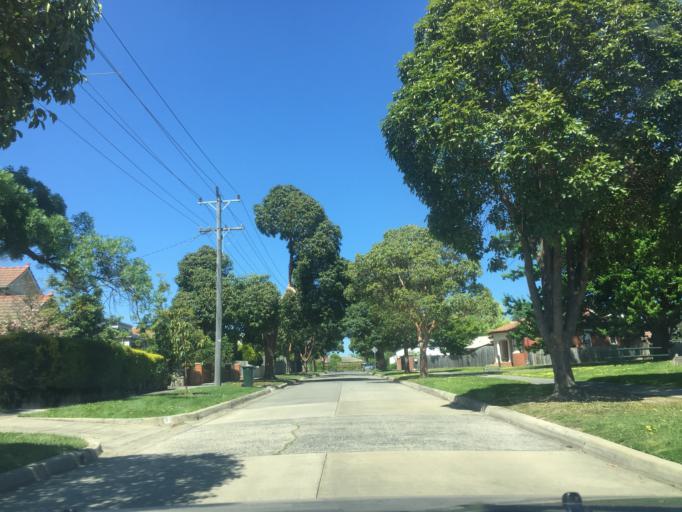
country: AU
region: Victoria
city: Mont Albert
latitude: -37.8170
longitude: 145.0955
